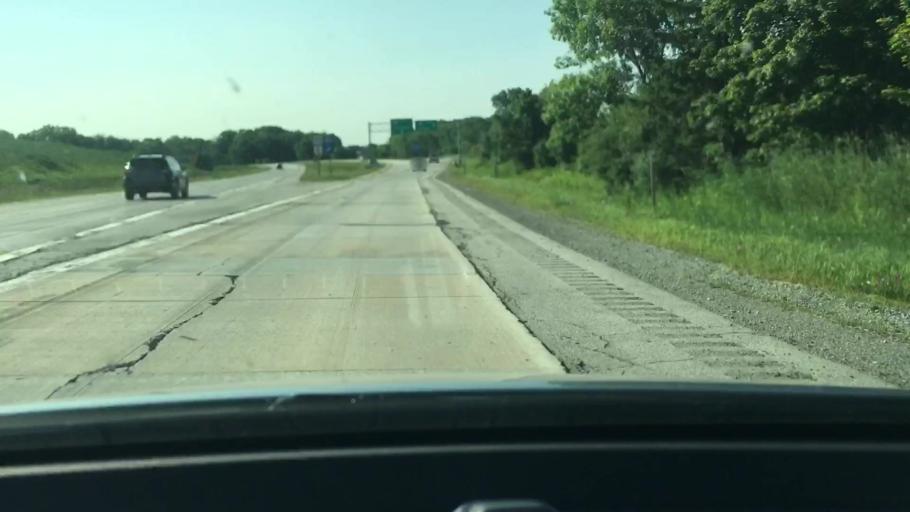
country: US
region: Wisconsin
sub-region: Brown County
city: Ashwaubenon
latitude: 44.4871
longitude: -88.0871
